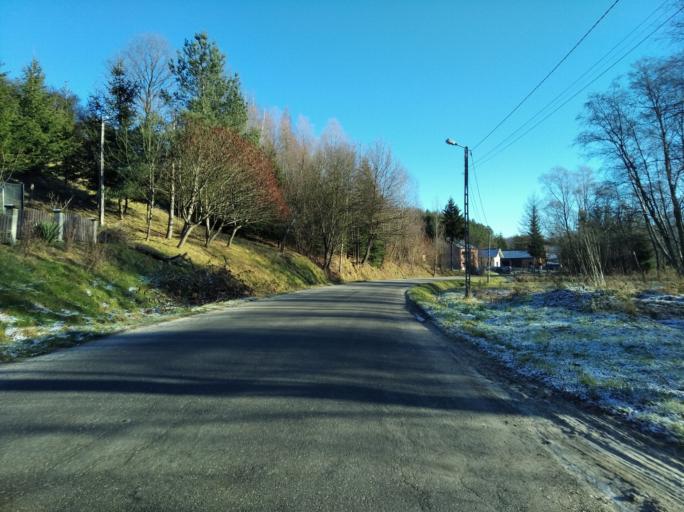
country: PL
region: Subcarpathian Voivodeship
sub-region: Powiat strzyzowski
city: Strzyzow
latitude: 49.9251
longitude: 21.7861
